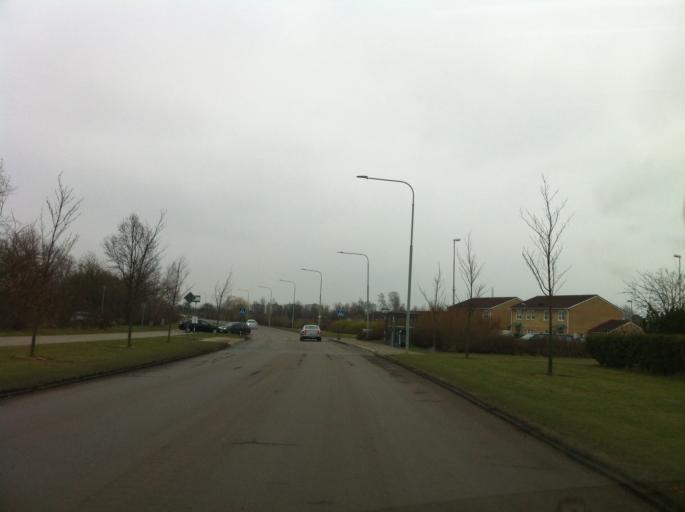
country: SE
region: Skane
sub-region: Landskrona
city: Landskrona
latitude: 55.8902
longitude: 12.8169
